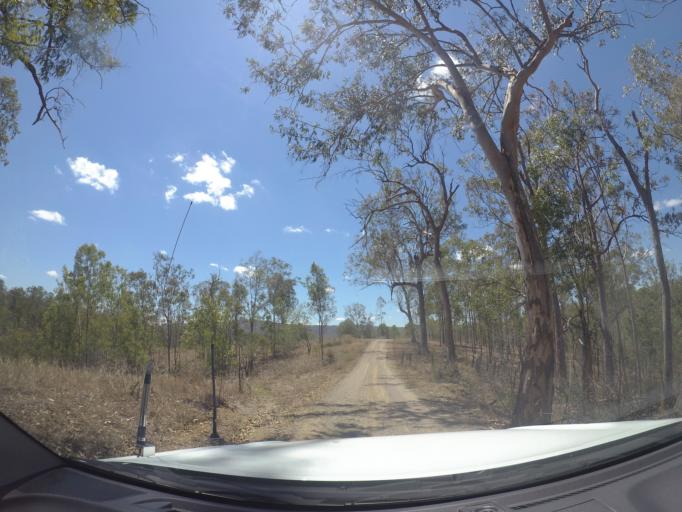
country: AU
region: Queensland
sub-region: Ipswich
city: Springfield Lakes
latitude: -27.8242
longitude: 152.8397
